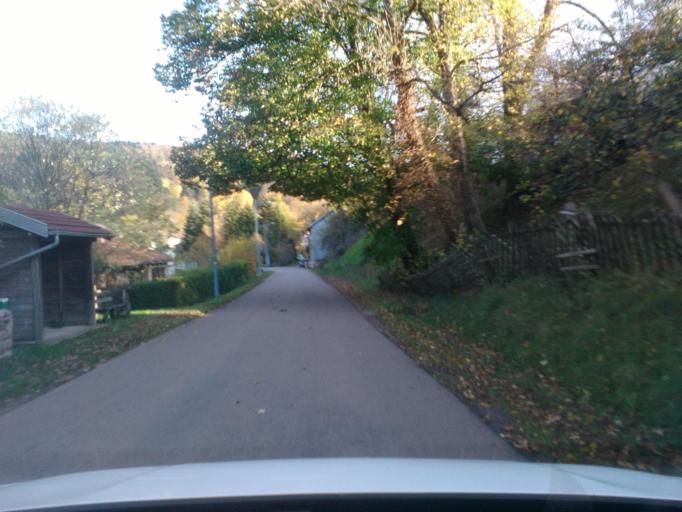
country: FR
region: Lorraine
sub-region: Departement des Vosges
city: Saint-Die-des-Vosges
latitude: 48.3328
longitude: 6.9883
